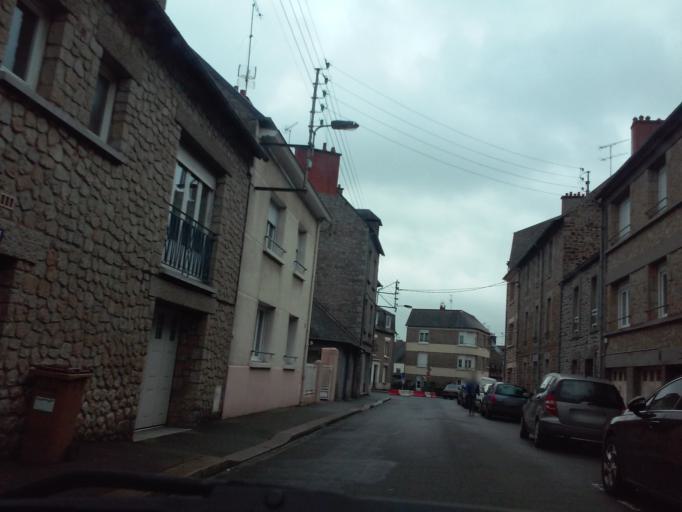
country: FR
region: Brittany
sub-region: Departement d'Ille-et-Vilaine
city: Fougeres
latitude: 48.3519
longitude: -1.1948
